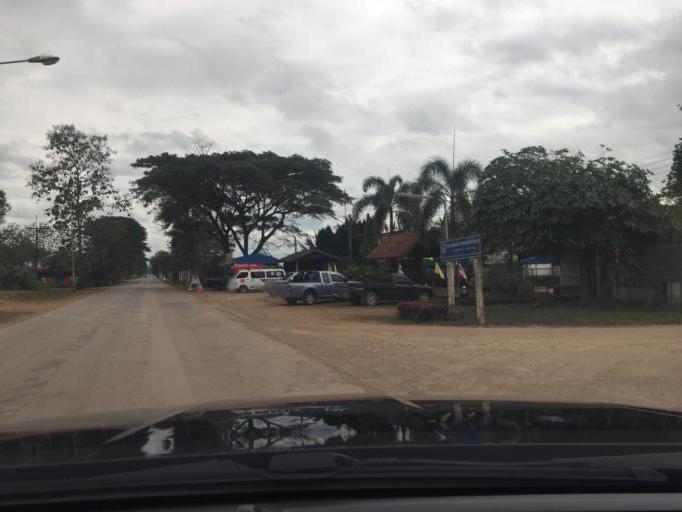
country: TH
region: Phayao
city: Pong
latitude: 19.1671
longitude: 100.3144
